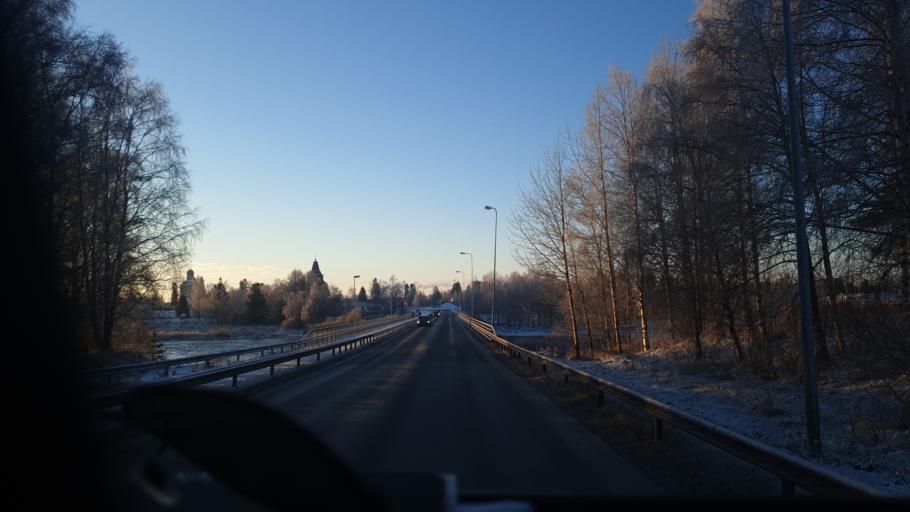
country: FI
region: Northern Ostrobothnia
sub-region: Ylivieska
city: Kalajoki
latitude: 64.2587
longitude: 23.9432
